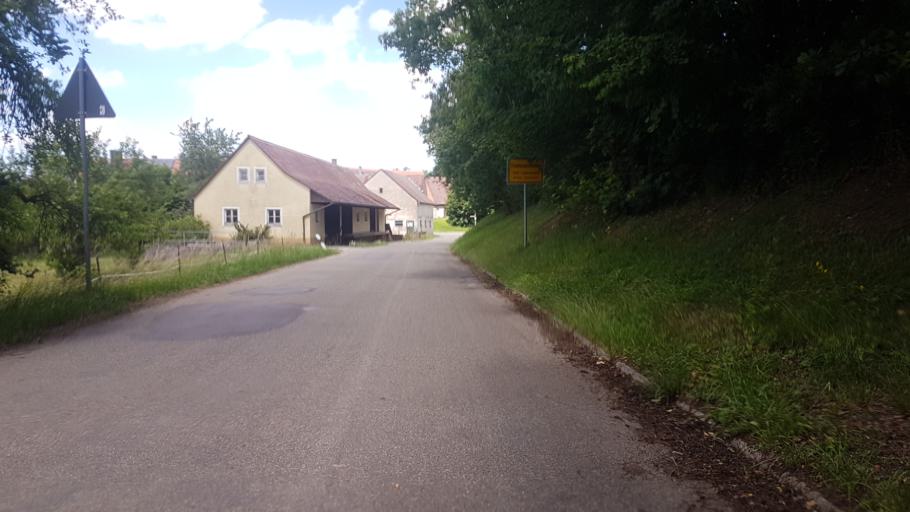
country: DE
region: Bavaria
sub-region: Regierungsbezirk Mittelfranken
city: Colmberg
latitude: 49.3356
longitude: 10.3757
